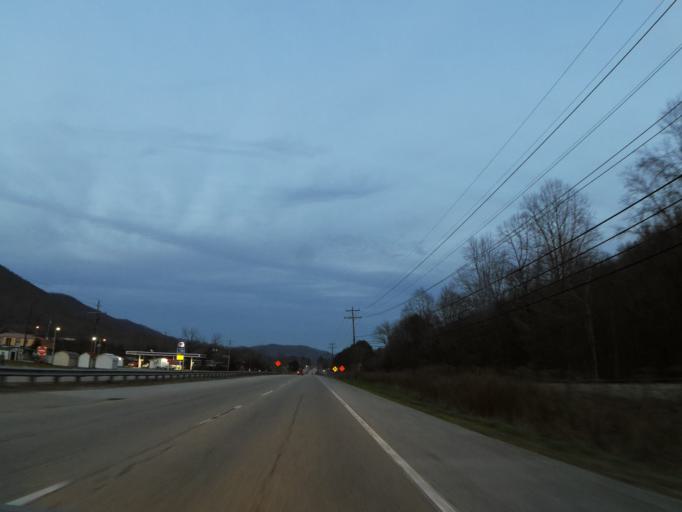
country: US
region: Tennessee
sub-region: Roane County
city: Harriman
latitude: 35.9649
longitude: -84.5165
